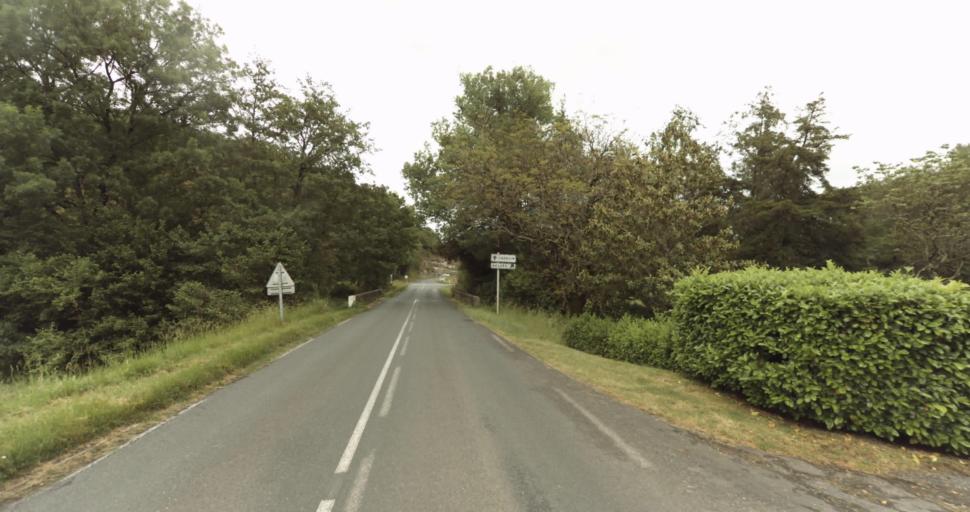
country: FR
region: Aquitaine
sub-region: Departement de la Dordogne
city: Beaumont-du-Perigord
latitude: 44.7707
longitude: 0.7981
